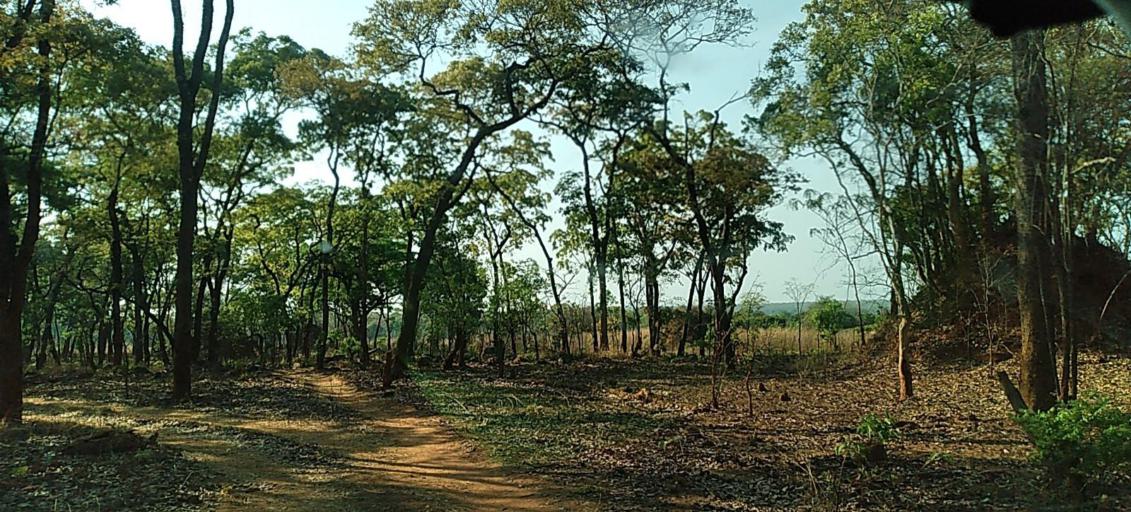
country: ZM
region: North-Western
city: Kalengwa
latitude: -13.2378
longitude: 25.0524
